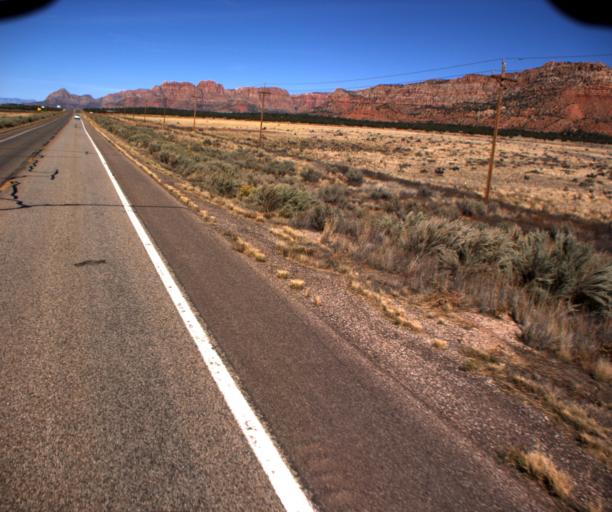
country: US
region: Arizona
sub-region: Mohave County
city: Colorado City
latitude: 36.9416
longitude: -112.9519
